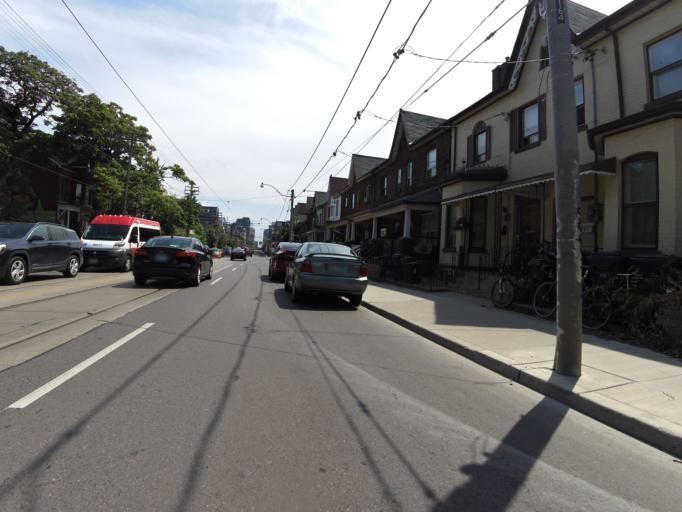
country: CA
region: Ontario
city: Toronto
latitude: 43.6500
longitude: -79.4052
